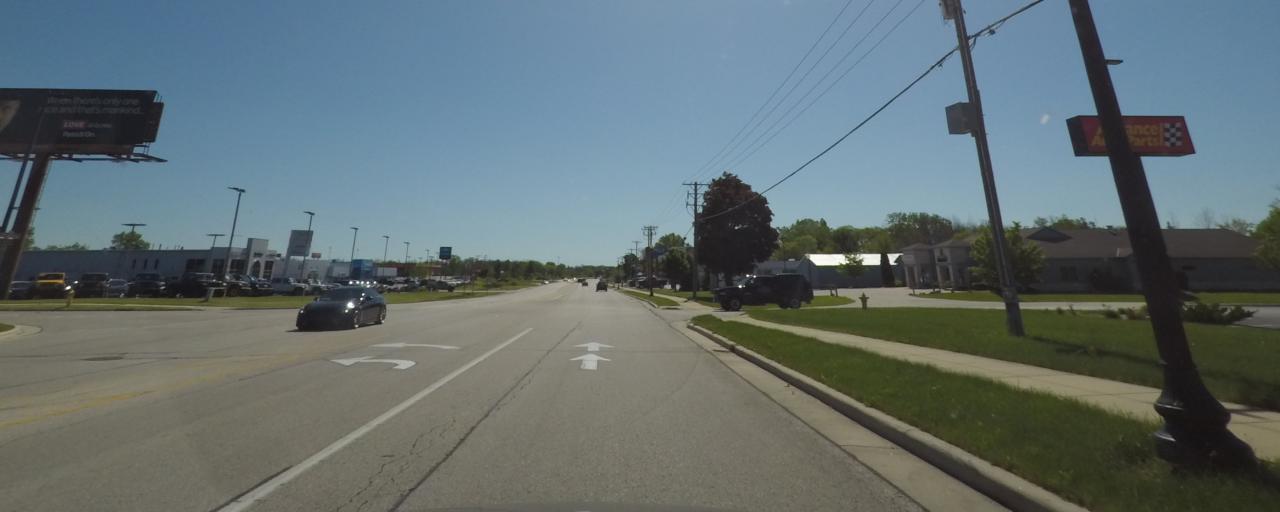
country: US
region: Wisconsin
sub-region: Sheboygan County
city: Plymouth
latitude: 43.7471
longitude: -87.9472
